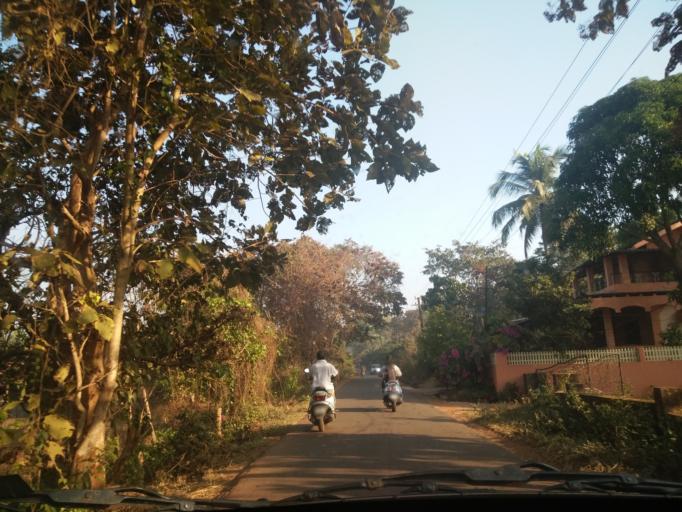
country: IN
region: Goa
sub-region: South Goa
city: Davorlim
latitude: 15.2825
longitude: 74.0066
